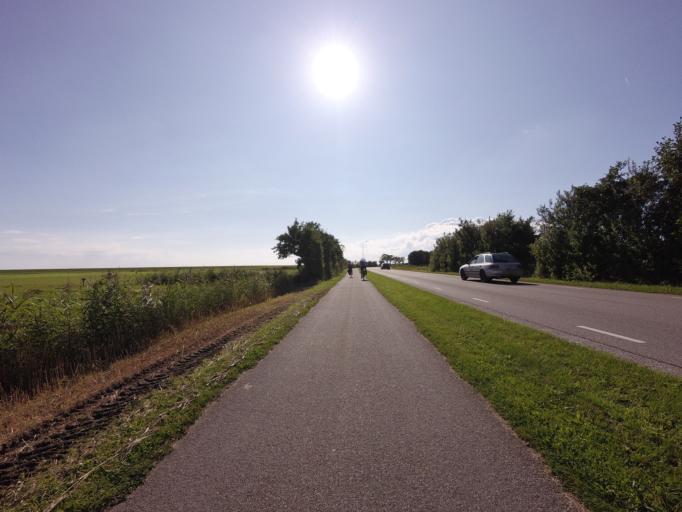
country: NL
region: Friesland
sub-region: Gemeente Terschelling
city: West-Terschelling
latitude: 53.3766
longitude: 5.2630
